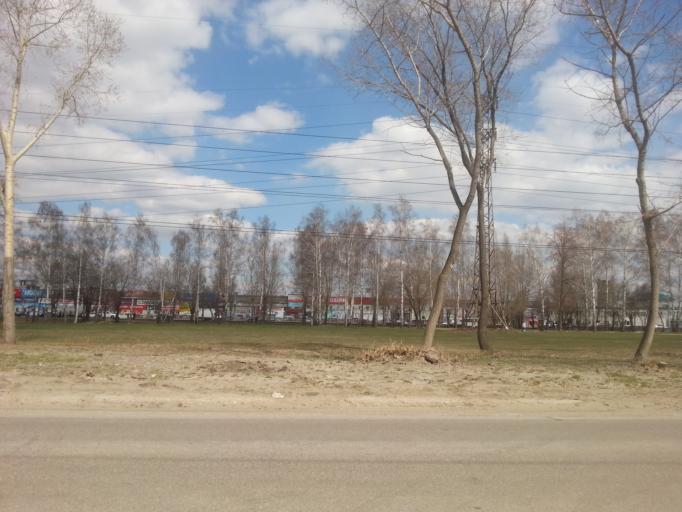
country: RU
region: Altai Krai
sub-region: Gorod Barnaulskiy
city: Barnaul
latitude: 53.3860
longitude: 83.7334
